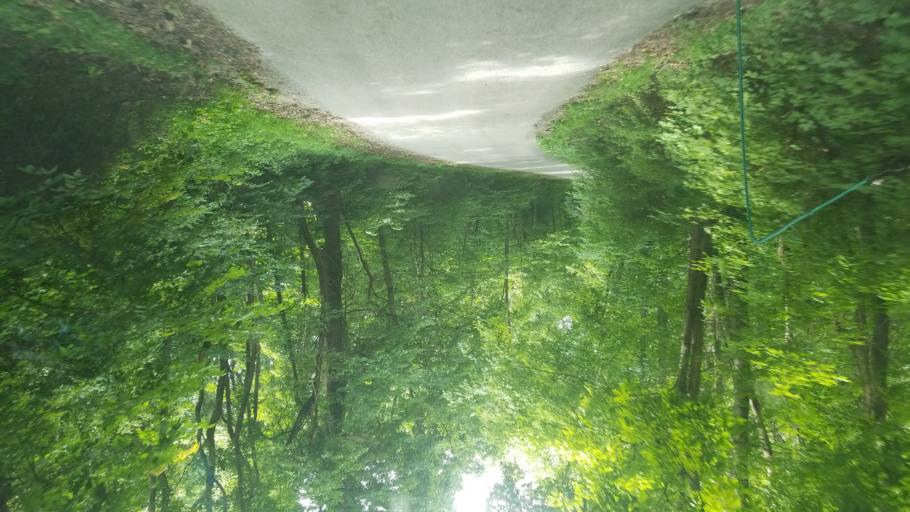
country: US
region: Illinois
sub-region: Jackson County
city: Murphysboro
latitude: 37.6228
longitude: -89.3688
